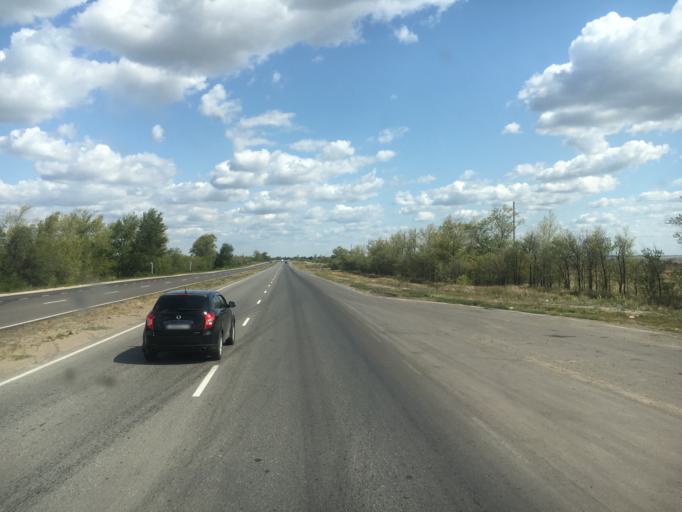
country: KZ
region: Qostanay
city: Kostanay
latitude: 53.1121
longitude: 63.5293
